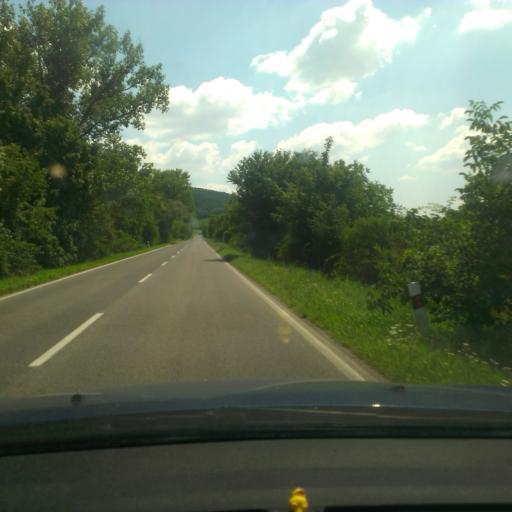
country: SK
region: Trnavsky
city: Hlohovec
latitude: 48.4667
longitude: 17.8129
